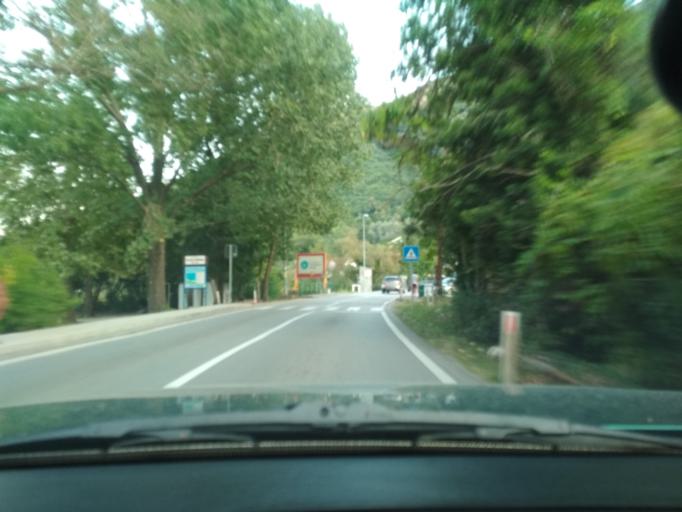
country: ME
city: Lipci
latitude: 42.4882
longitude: 18.6507
